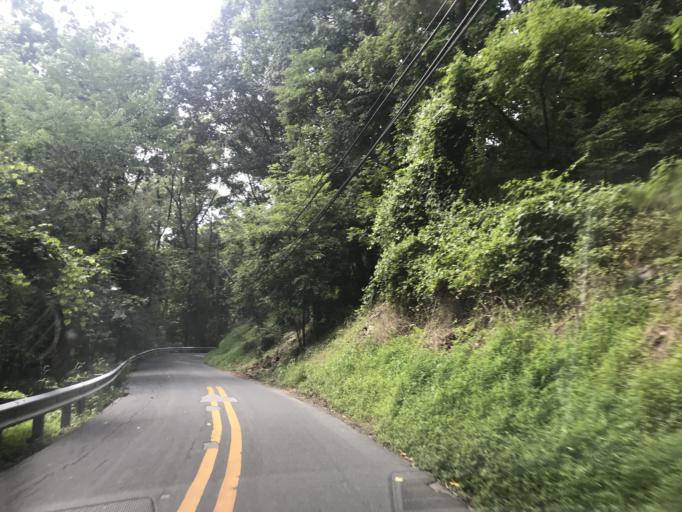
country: US
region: Delaware
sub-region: New Castle County
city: Greenville
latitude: 39.7641
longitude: -75.6361
